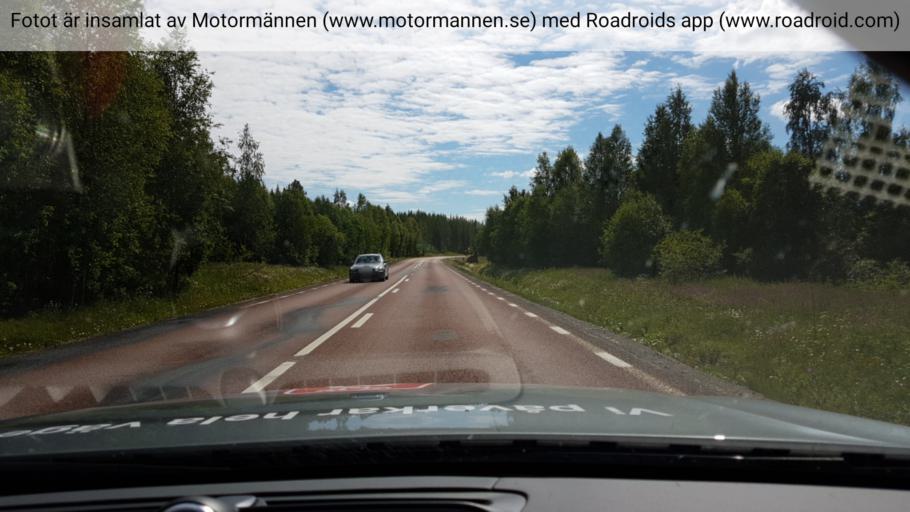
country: SE
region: Jaemtland
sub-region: Stroemsunds Kommun
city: Stroemsund
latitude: 63.9797
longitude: 15.8708
